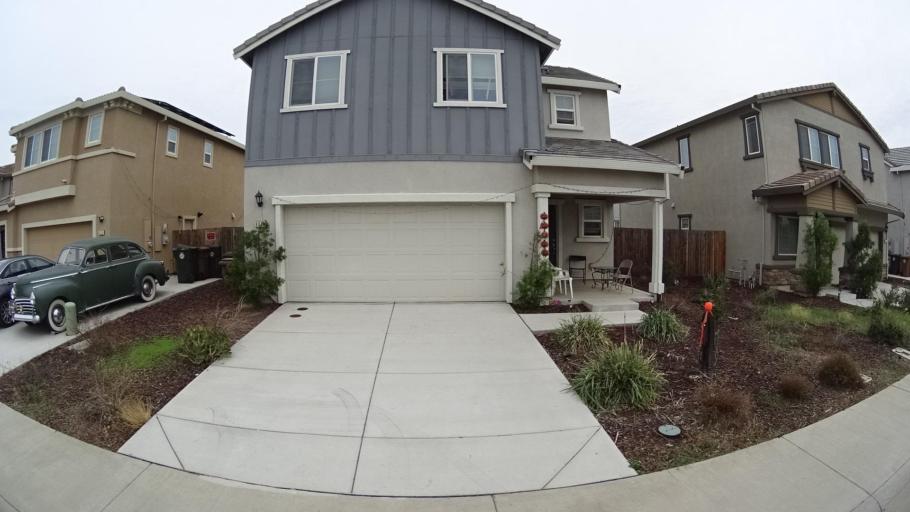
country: US
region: California
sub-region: Sacramento County
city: Laguna
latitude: 38.4466
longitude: -121.4029
